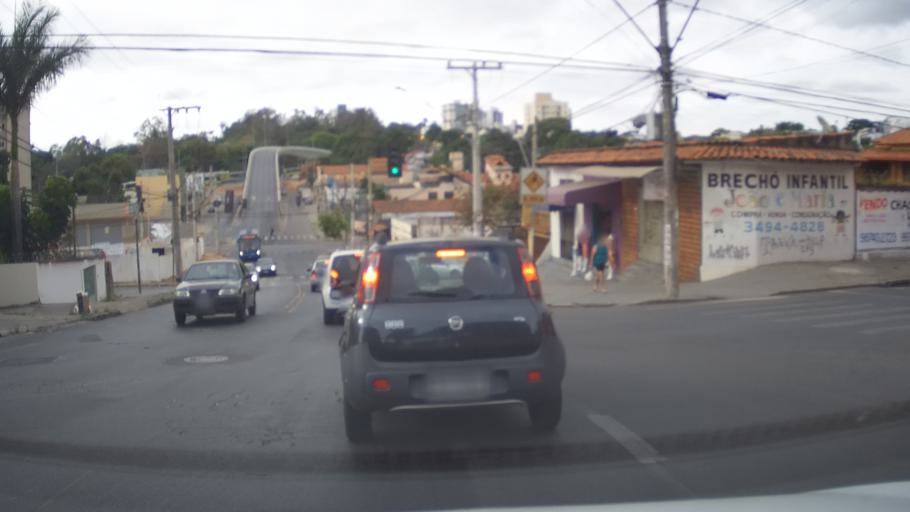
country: BR
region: Minas Gerais
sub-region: Belo Horizonte
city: Belo Horizonte
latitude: -19.8277
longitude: -43.9630
